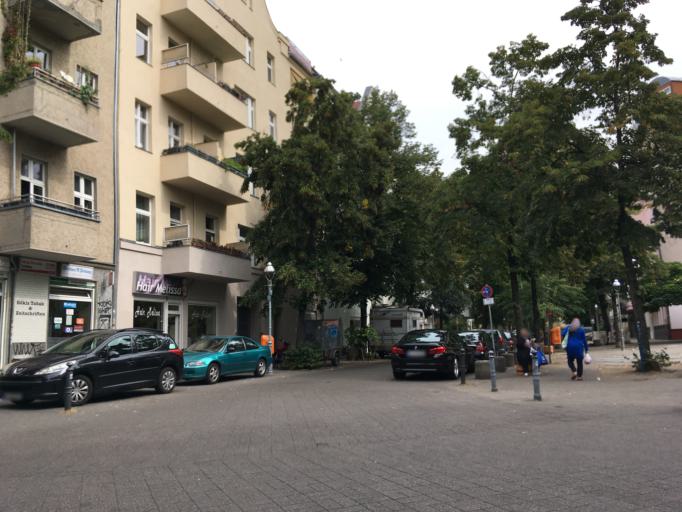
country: DE
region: Berlin
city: Wedding Bezirk
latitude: 52.5508
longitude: 13.3594
